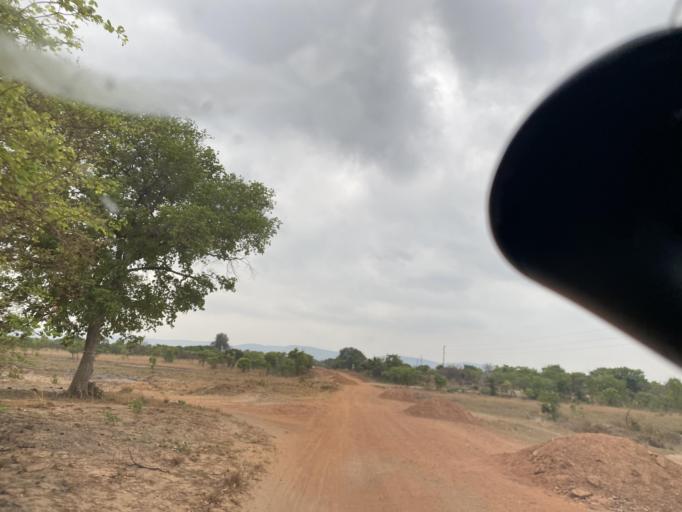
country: ZM
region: Lusaka
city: Chongwe
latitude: -15.2521
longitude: 28.7276
